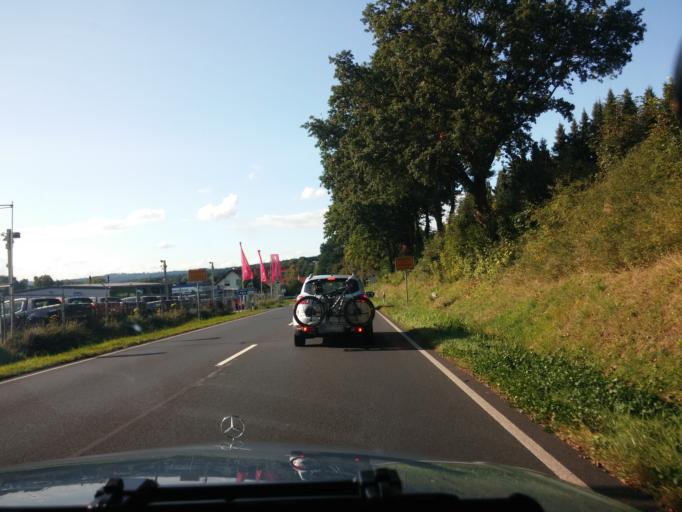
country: DE
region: Hesse
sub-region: Regierungsbezirk Kassel
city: Eichenzell
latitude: 50.4643
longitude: 9.7105
